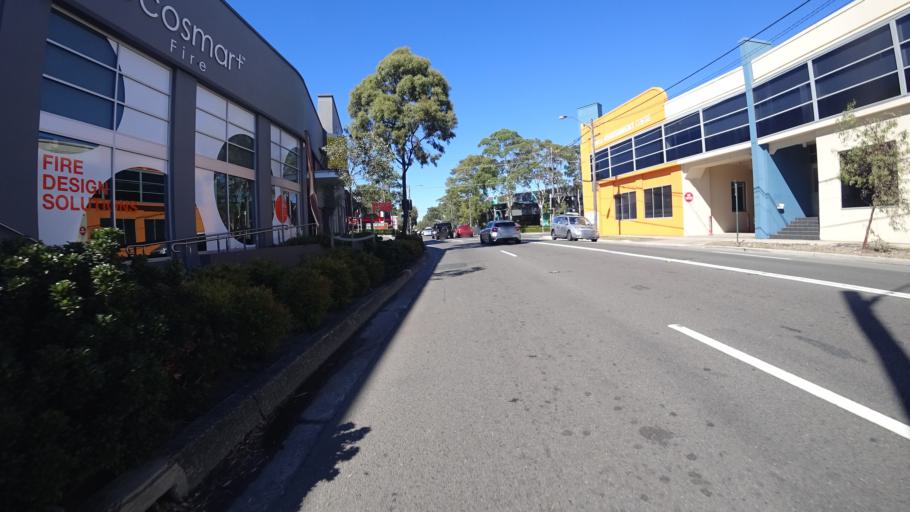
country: AU
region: New South Wales
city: Alexandria
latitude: -33.9112
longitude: 151.1979
